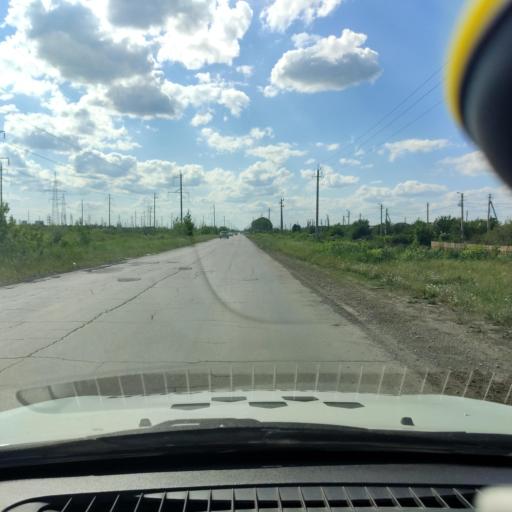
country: RU
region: Samara
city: Tol'yatti
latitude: 53.5895
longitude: 49.3154
